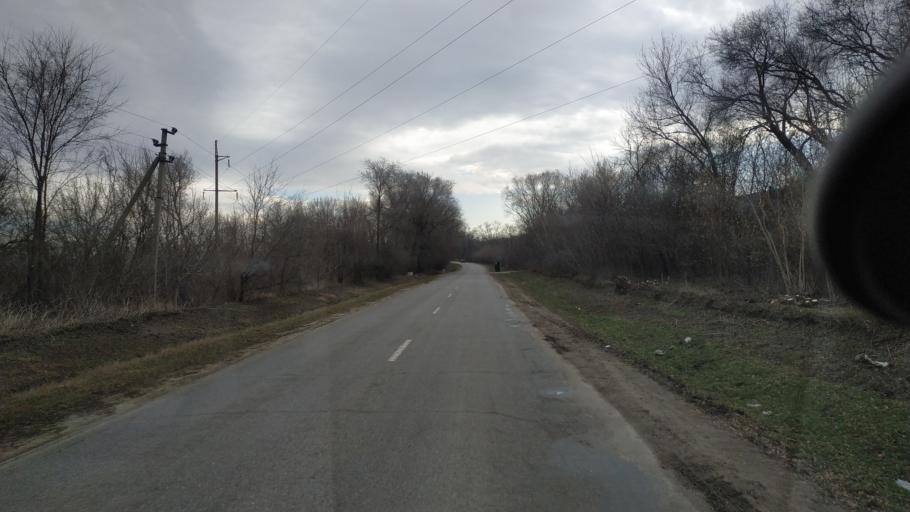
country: MD
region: Chisinau
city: Vadul lui Voda
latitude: 47.1320
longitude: 29.0619
